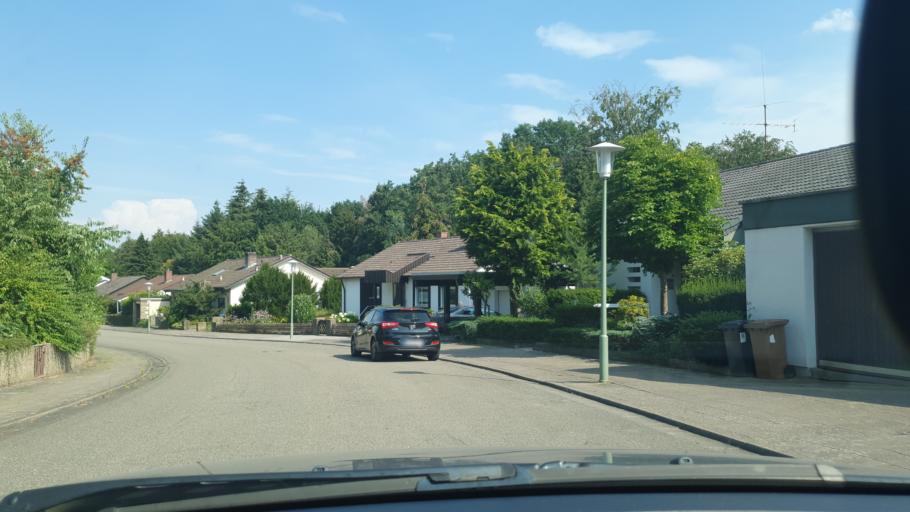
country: DE
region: Rheinland-Pfalz
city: Stelzenberg
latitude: 49.4279
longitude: 7.7245
